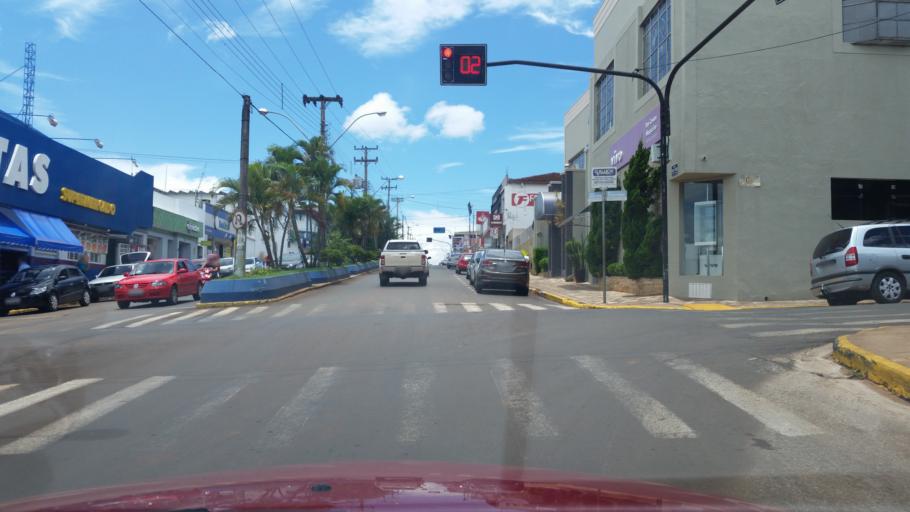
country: BR
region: Sao Paulo
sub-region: Itai
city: Itai
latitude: -23.4194
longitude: -49.0924
